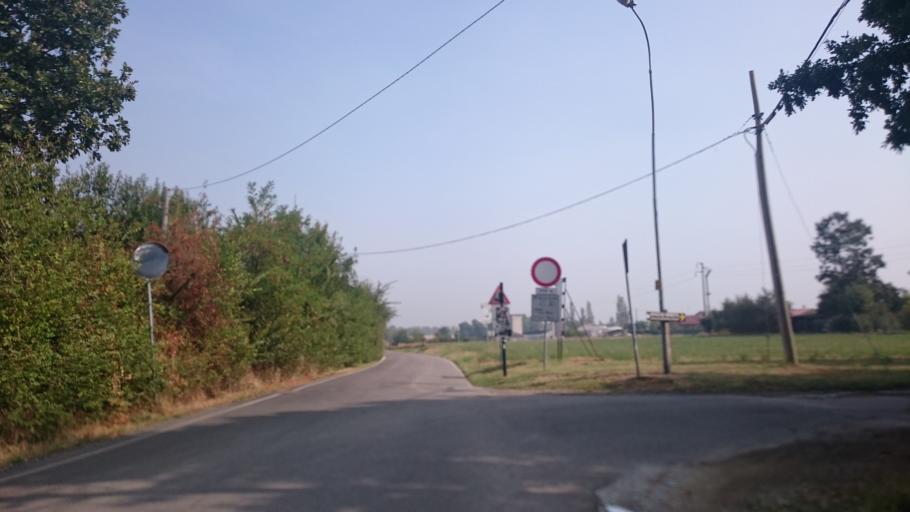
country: IT
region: Emilia-Romagna
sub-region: Provincia di Reggio Emilia
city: Fogliano
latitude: 44.6575
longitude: 10.6294
